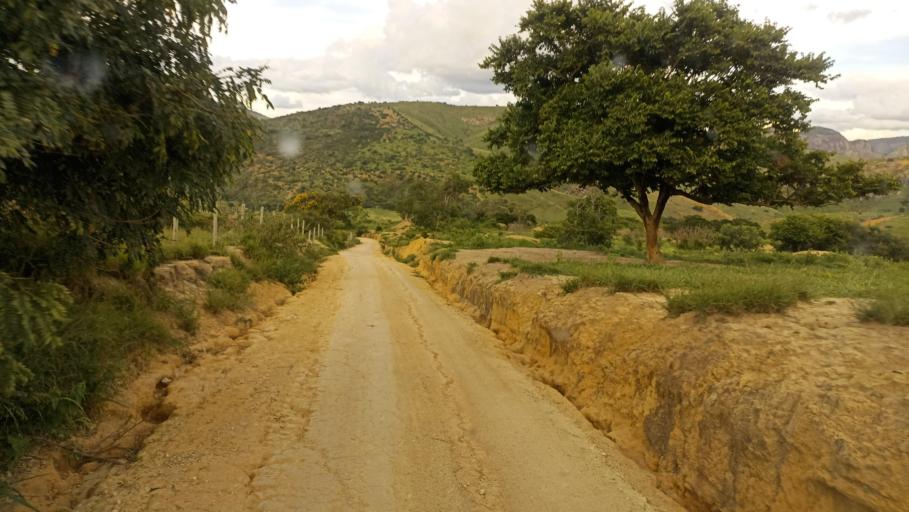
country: BR
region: Minas Gerais
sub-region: Almenara
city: Almenara
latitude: -16.5421
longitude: -40.4464
